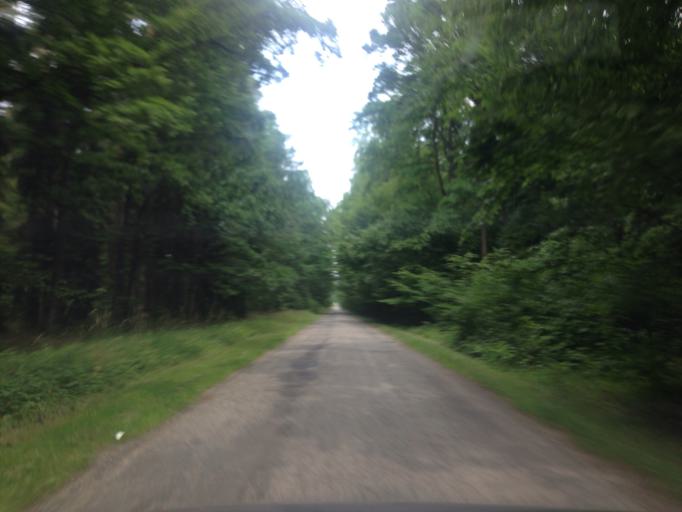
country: PL
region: Kujawsko-Pomorskie
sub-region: Powiat golubsko-dobrzynski
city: Radomin
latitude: 53.1574
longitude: 19.1525
